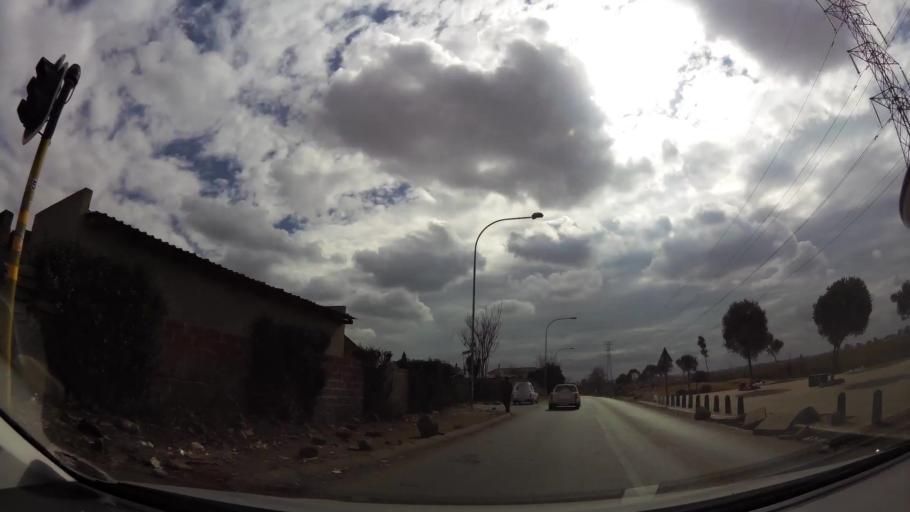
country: ZA
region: Gauteng
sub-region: City of Johannesburg Metropolitan Municipality
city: Soweto
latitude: -26.2723
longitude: 27.8815
